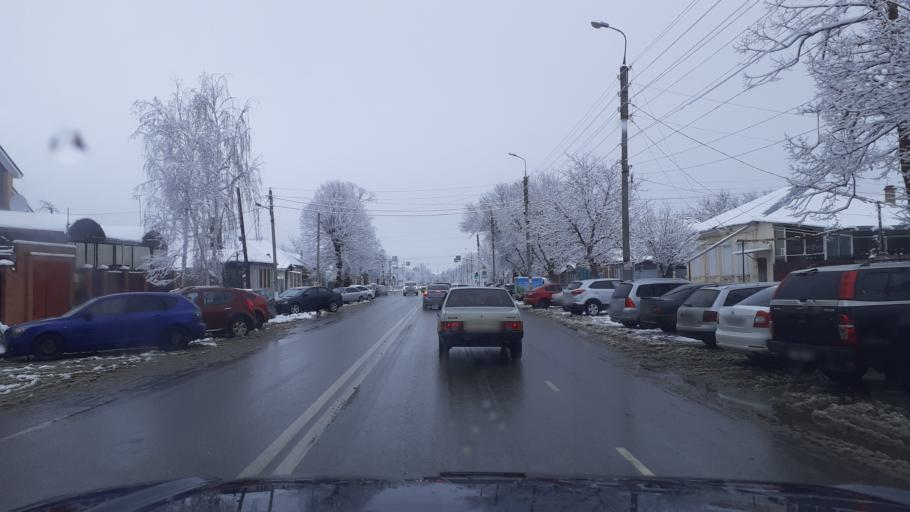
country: RU
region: Adygeya
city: Maykop
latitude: 44.6106
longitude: 40.1124
